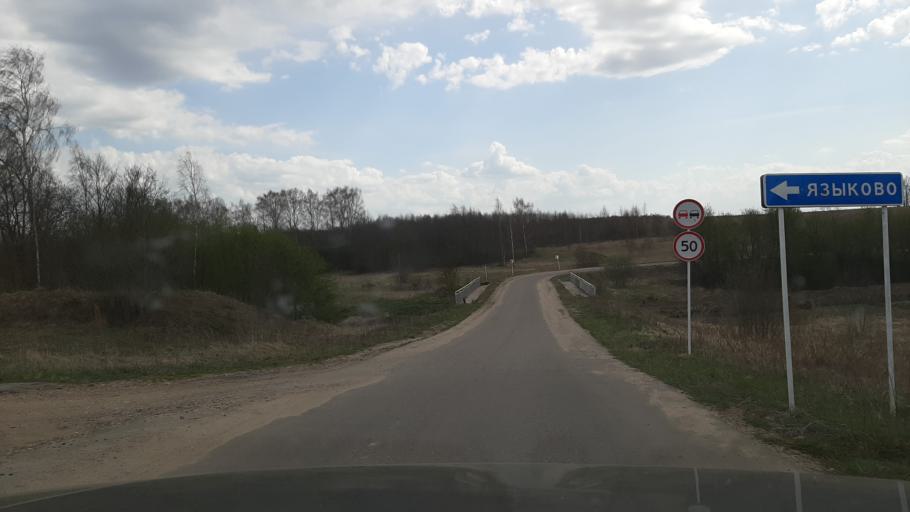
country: RU
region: Ivanovo
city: Furmanov
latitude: 57.3168
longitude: 41.1664
